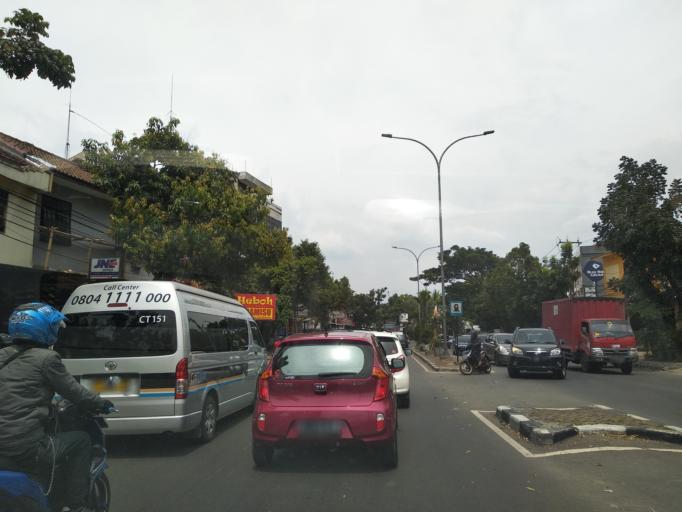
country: ID
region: West Java
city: Bandung
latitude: -6.9570
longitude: 107.6395
